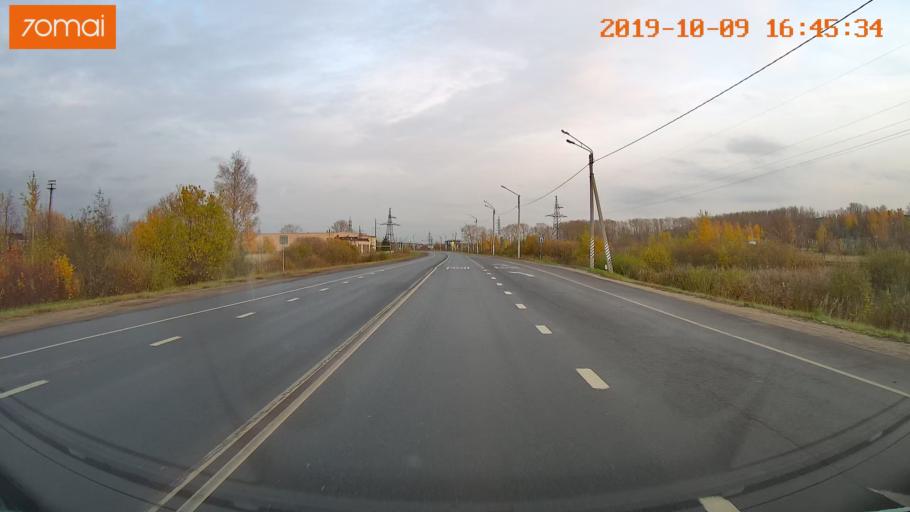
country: RU
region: Kostroma
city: Volgorechensk
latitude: 57.4458
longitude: 41.1570
